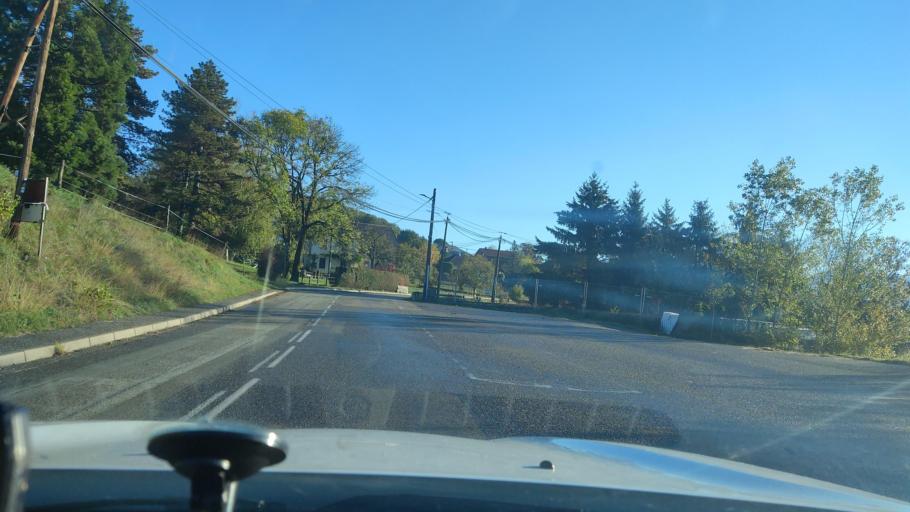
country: FR
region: Rhone-Alpes
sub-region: Departement de la Savoie
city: Cruet
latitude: 45.5290
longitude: 6.0928
